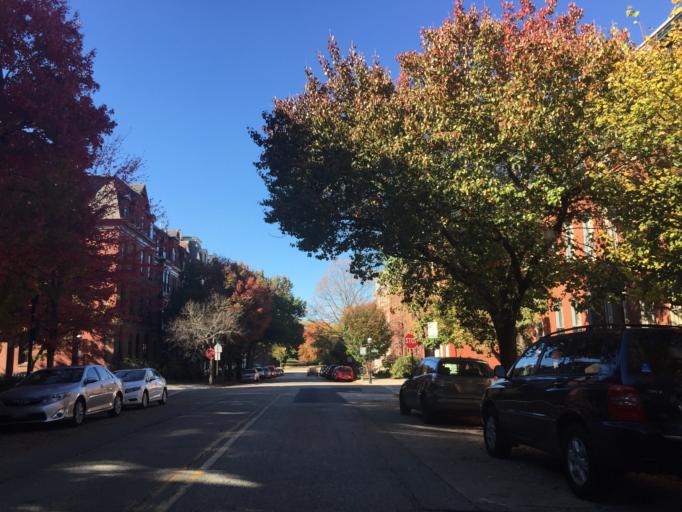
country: US
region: Maryland
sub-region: City of Baltimore
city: Baltimore
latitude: 39.3074
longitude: -76.6246
